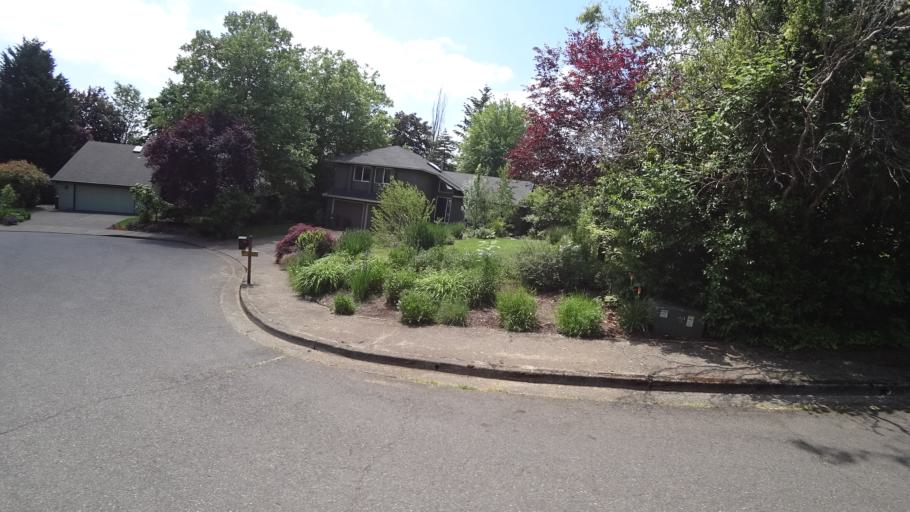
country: US
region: Oregon
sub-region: Clackamas County
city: Lake Oswego
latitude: 45.4350
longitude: -122.7040
